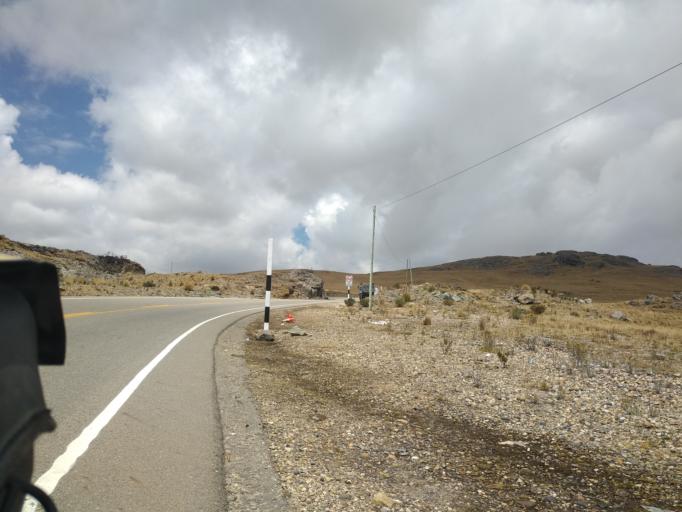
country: PE
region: La Libertad
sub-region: Provincia de Santiago de Chuco
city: Quiruvilca
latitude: -7.9492
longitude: -78.1912
